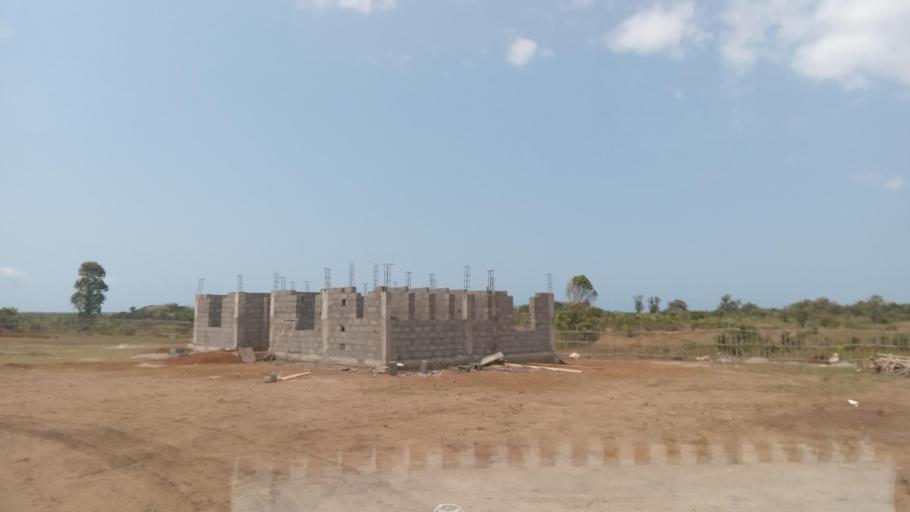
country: MG
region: Atsimo-Atsinanana
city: Vohipaho
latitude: -23.8329
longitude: 47.5533
